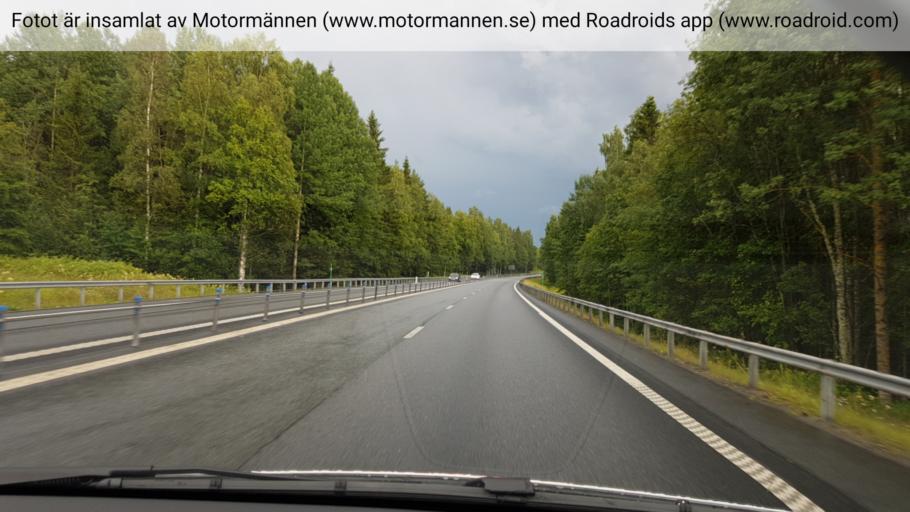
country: SE
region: Vaesterbotten
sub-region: Vannas Kommun
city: Vannasby
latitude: 63.9125
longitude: 19.8845
